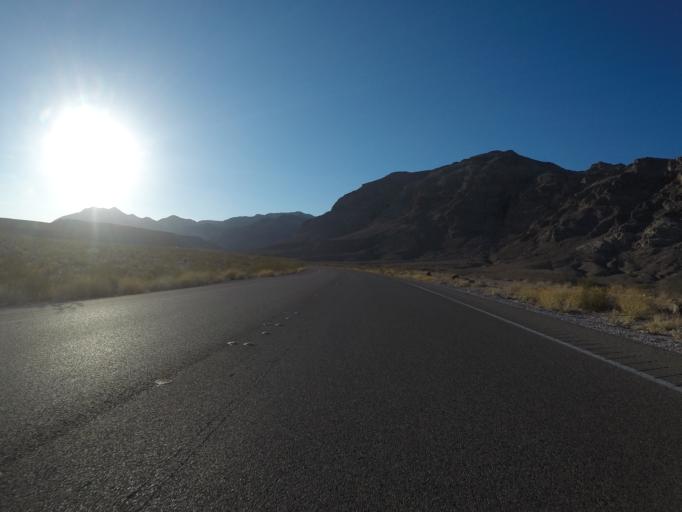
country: US
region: Nevada
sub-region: Clark County
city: Moapa Valley
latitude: 36.3660
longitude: -114.4581
